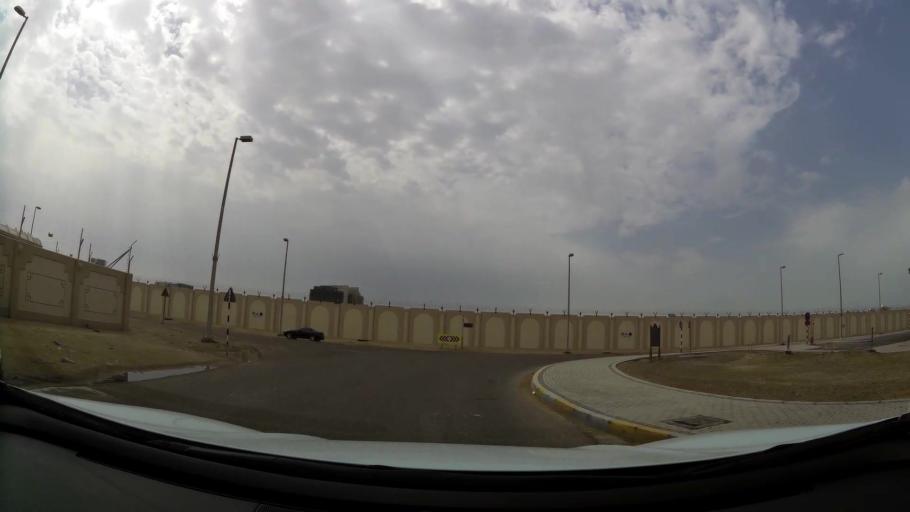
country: AE
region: Abu Dhabi
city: Abu Dhabi
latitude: 24.4288
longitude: 54.4609
